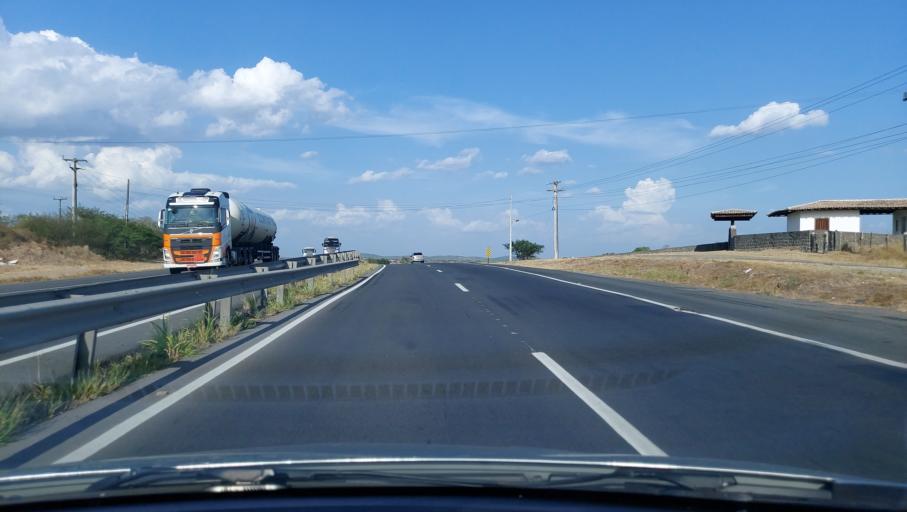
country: BR
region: Bahia
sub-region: Santo Estevao
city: Santo Estevao
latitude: -12.3806
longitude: -39.1274
